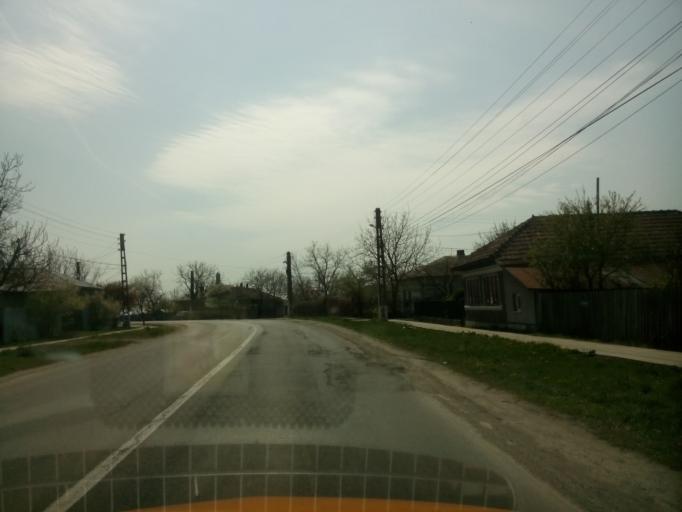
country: RO
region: Calarasi
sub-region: Comuna Soldanu
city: Negoesti
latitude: 44.2302
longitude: 26.5046
